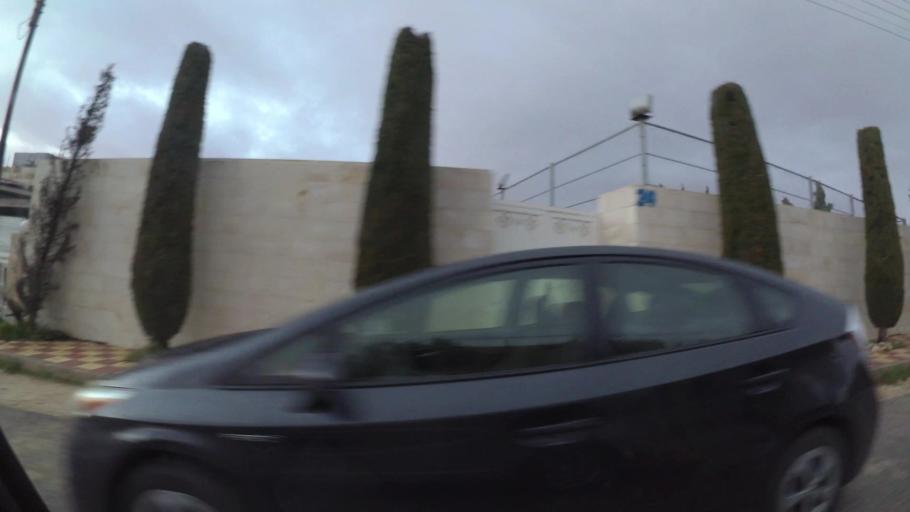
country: JO
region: Amman
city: Al Jubayhah
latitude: 32.0336
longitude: 35.8180
